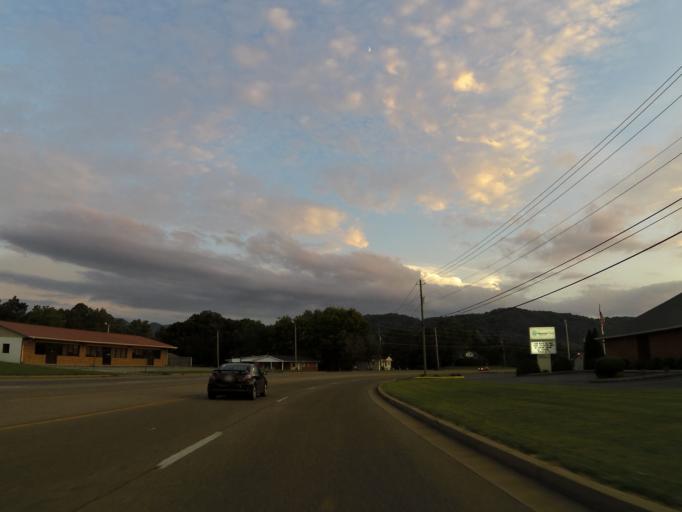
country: US
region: Tennessee
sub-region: Carter County
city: Hunter
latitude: 36.3713
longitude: -82.1575
